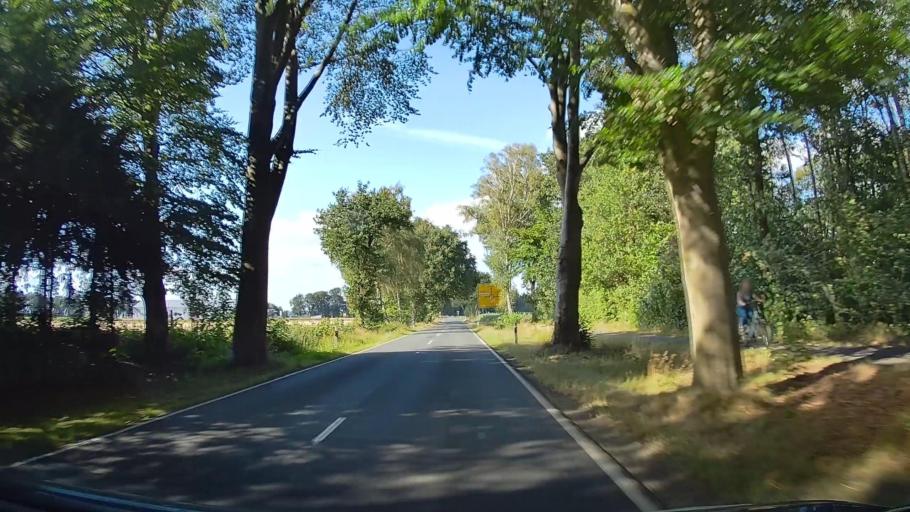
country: DE
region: Lower Saxony
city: Vrees
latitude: 52.8291
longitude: 7.7843
